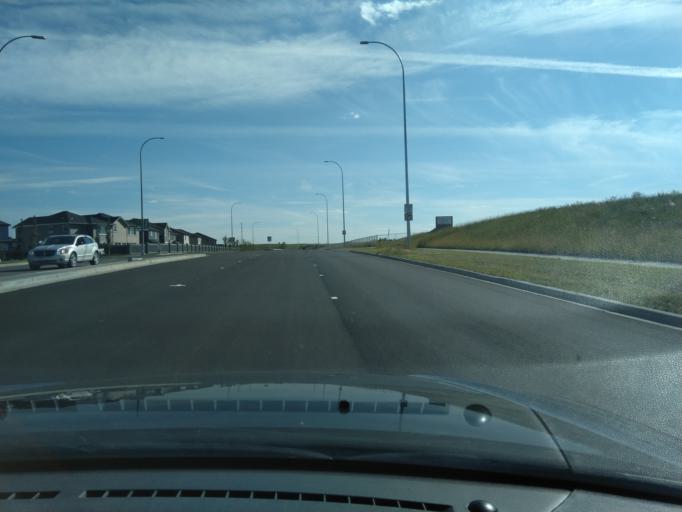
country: CA
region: Alberta
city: Calgary
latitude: 51.1765
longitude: -114.1761
